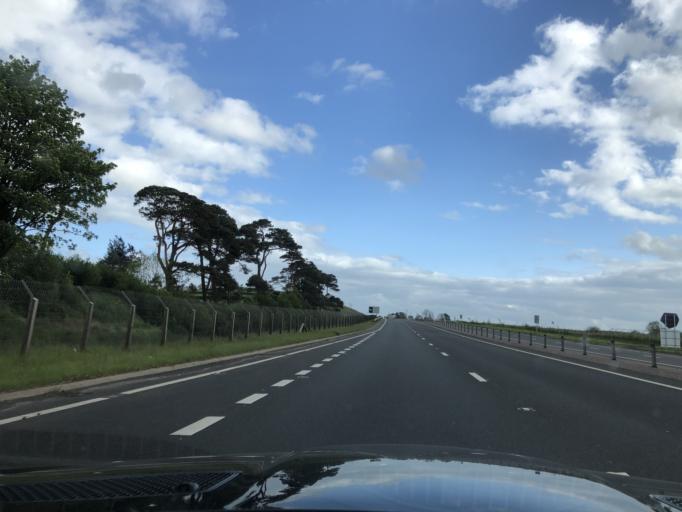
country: GB
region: Northern Ireland
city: Dunloy
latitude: 54.9824
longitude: -6.3478
